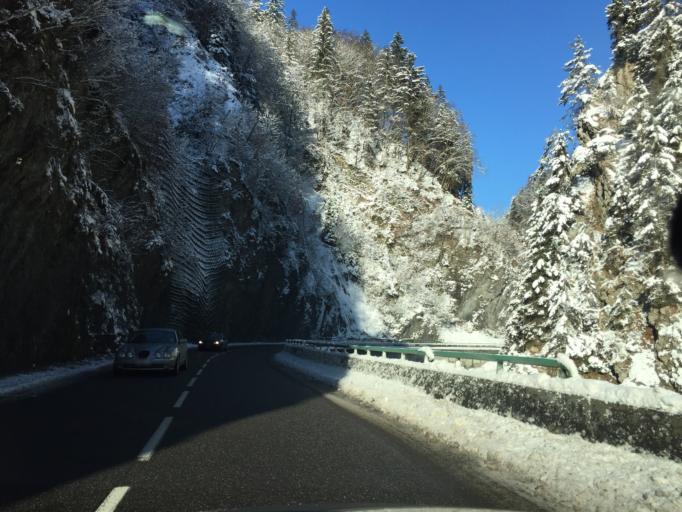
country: FR
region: Rhone-Alpes
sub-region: Departement de la Haute-Savoie
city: Feternes
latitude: 46.3299
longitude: 6.5818
